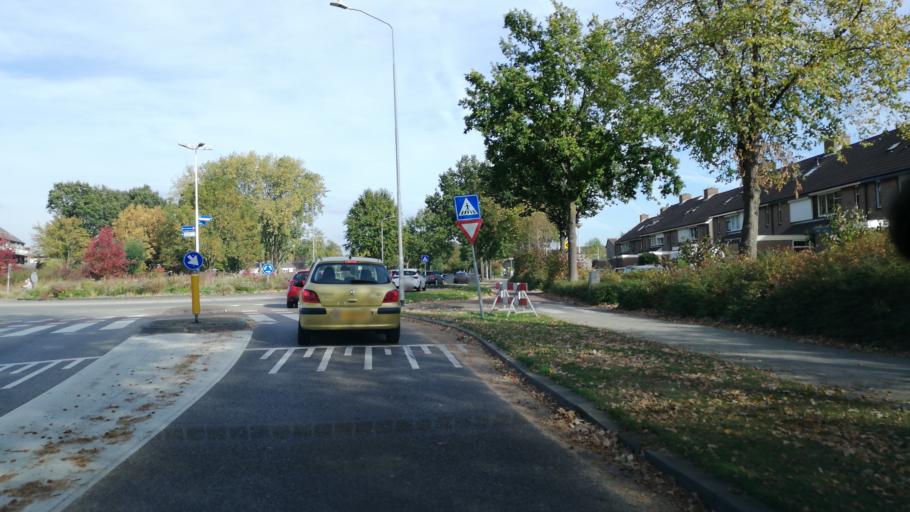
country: NL
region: Gelderland
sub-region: Gemeente Westervoort
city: Westervoort
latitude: 51.9534
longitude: 5.9791
